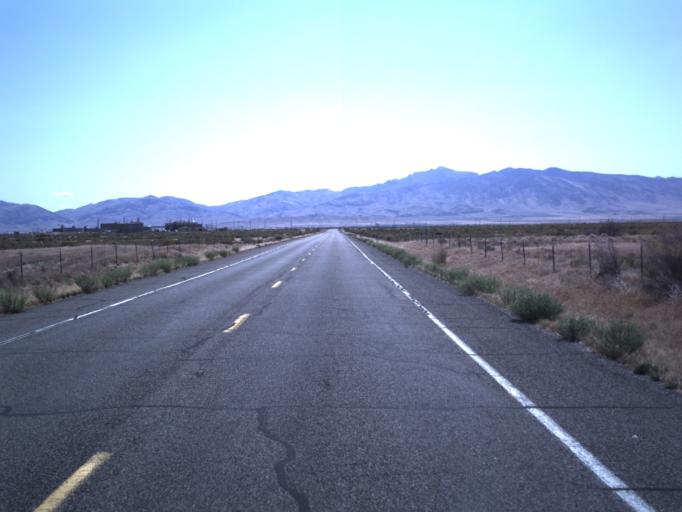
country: US
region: Utah
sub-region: Millard County
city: Delta
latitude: 39.4686
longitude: -112.4529
